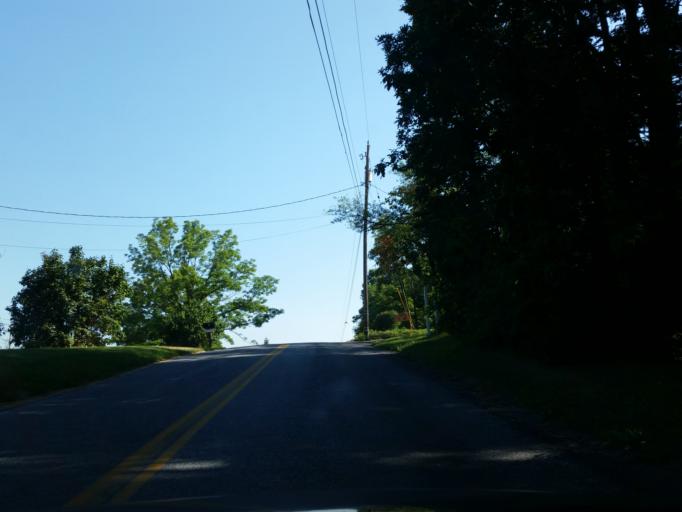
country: US
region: Pennsylvania
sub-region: Lebanon County
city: Palmyra
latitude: 40.3931
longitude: -76.6162
